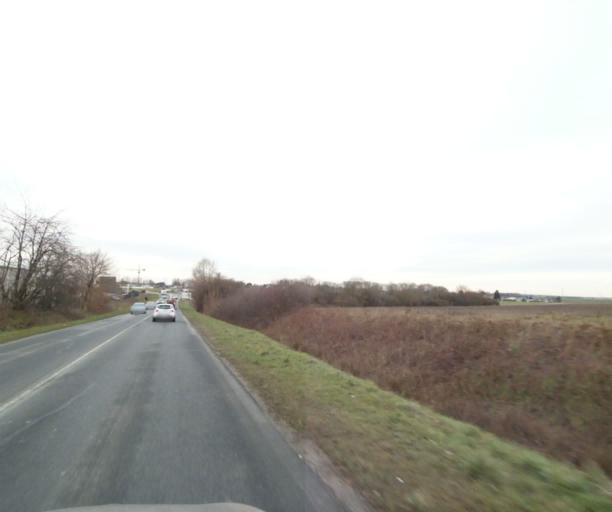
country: FR
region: Ile-de-France
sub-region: Departement de Seine-et-Marne
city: Othis
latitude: 49.0671
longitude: 2.6834
